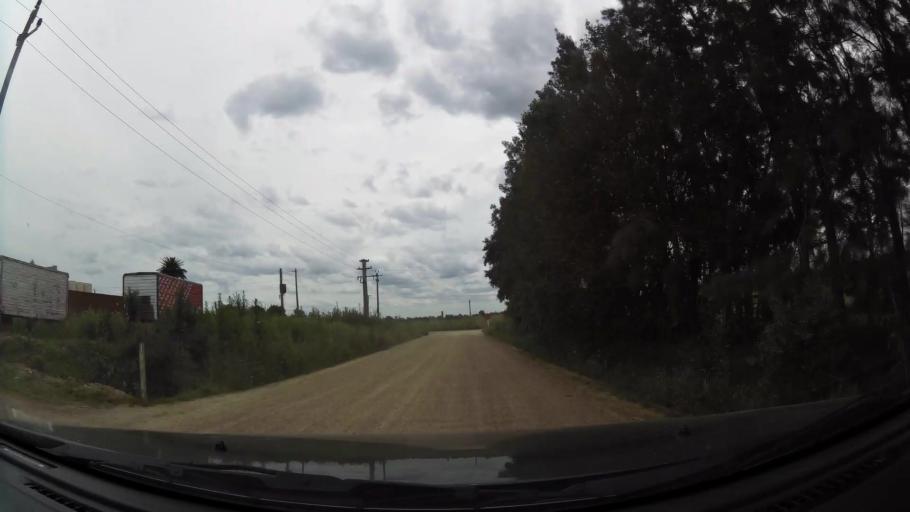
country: UY
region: Canelones
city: Las Piedras
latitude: -34.7082
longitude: -56.2053
